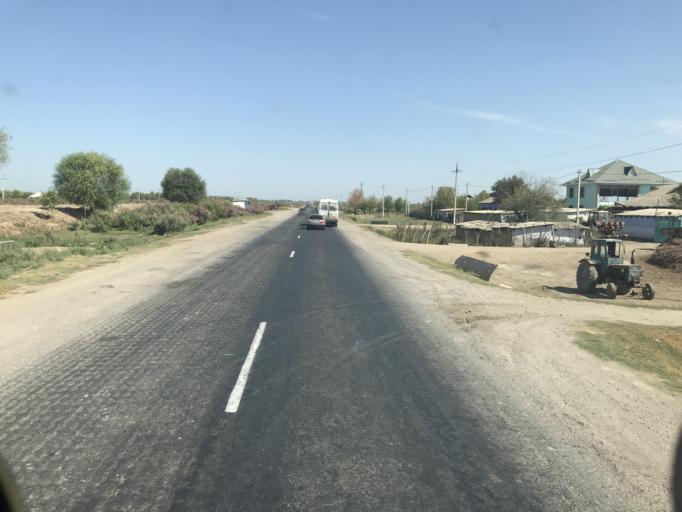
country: KZ
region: Ongtustik Qazaqstan
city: Myrzakent
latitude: 40.7316
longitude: 68.5365
